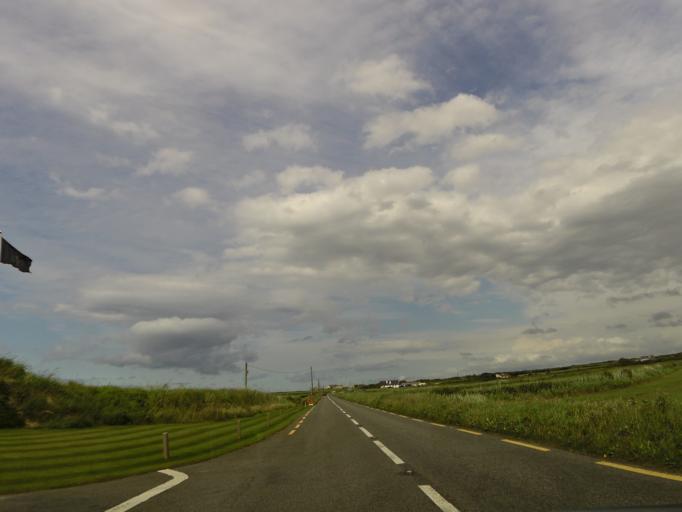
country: IE
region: Munster
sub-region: An Clar
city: Kilrush
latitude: 52.7584
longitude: -9.4762
